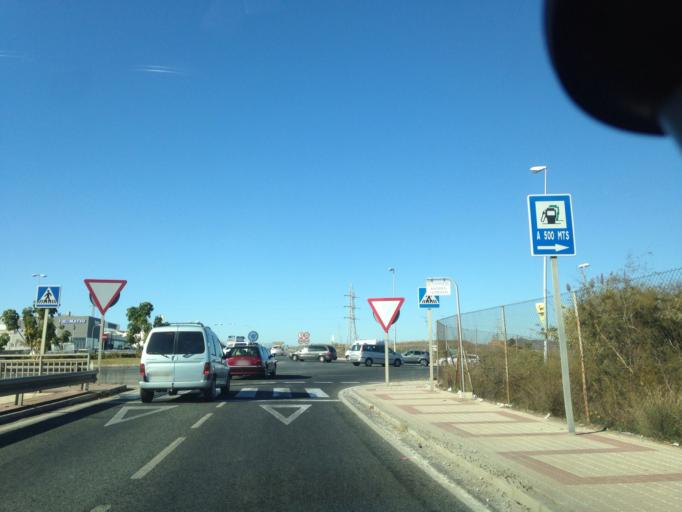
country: ES
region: Andalusia
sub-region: Provincia de Malaga
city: Malaga
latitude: 36.7142
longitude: -4.4823
